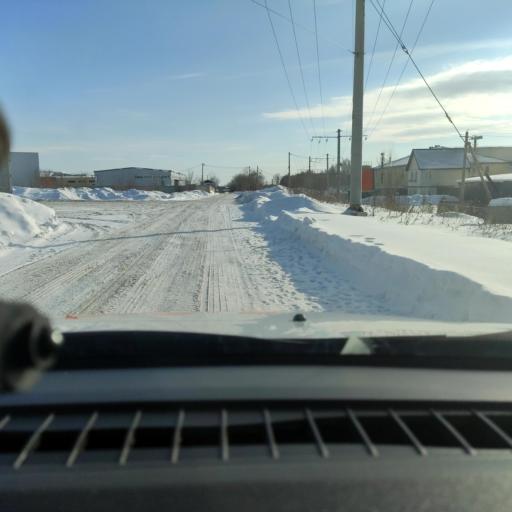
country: RU
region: Samara
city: Petra-Dubrava
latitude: 53.2627
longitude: 50.3525
